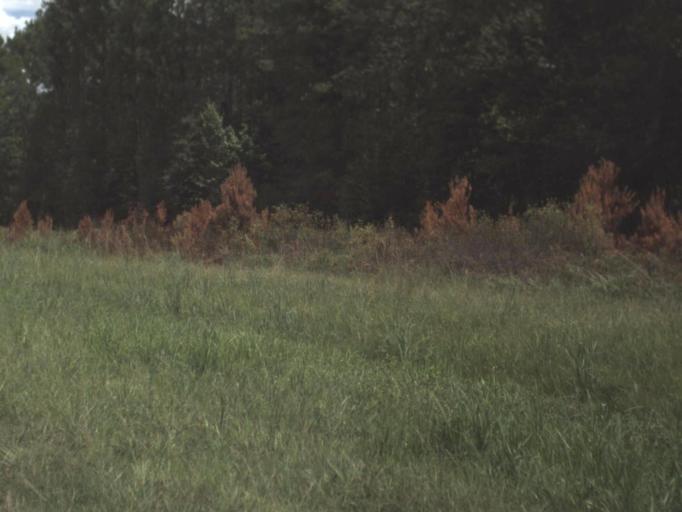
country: US
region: Florida
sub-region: Union County
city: Lake Butler
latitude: 29.9173
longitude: -82.4029
